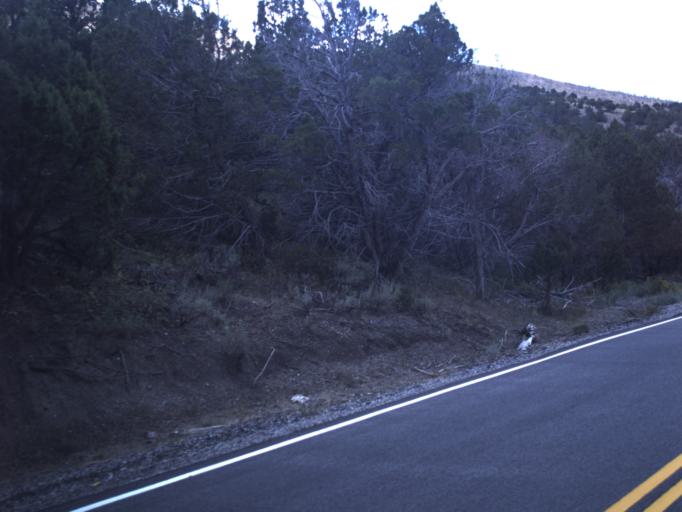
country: US
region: Utah
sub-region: Tooele County
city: Grantsville
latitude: 40.3426
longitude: -112.5806
